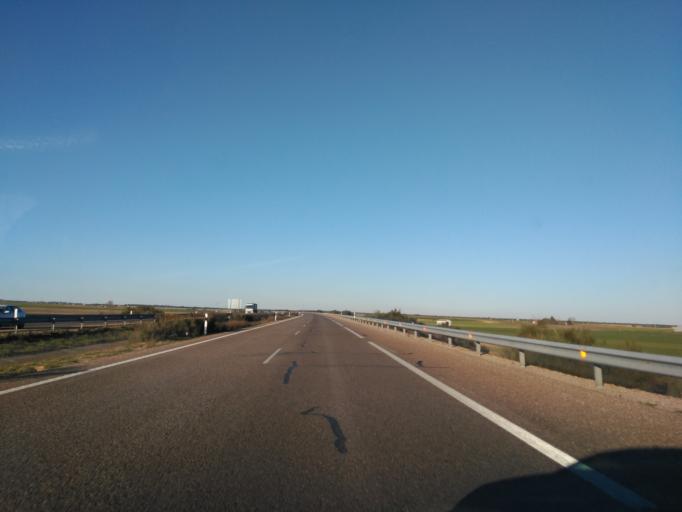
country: ES
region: Castille and Leon
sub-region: Provincia de Salamanca
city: Pajares de la Laguna
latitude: 41.1025
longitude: -5.4961
